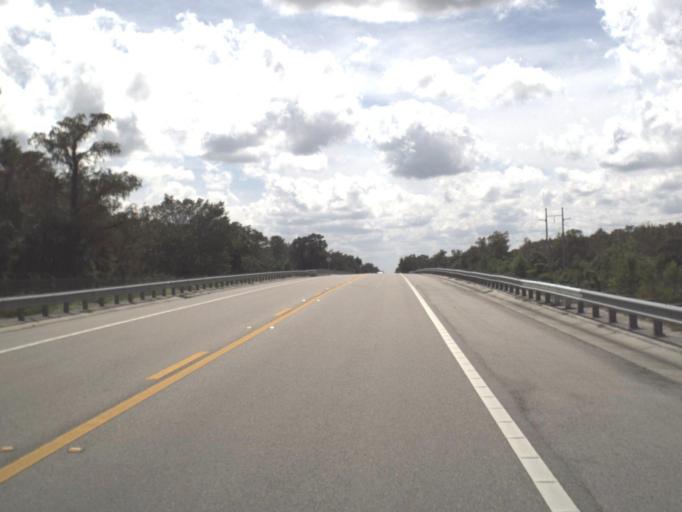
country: US
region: Florida
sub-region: Collier County
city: Immokalee
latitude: 26.2480
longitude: -81.3420
